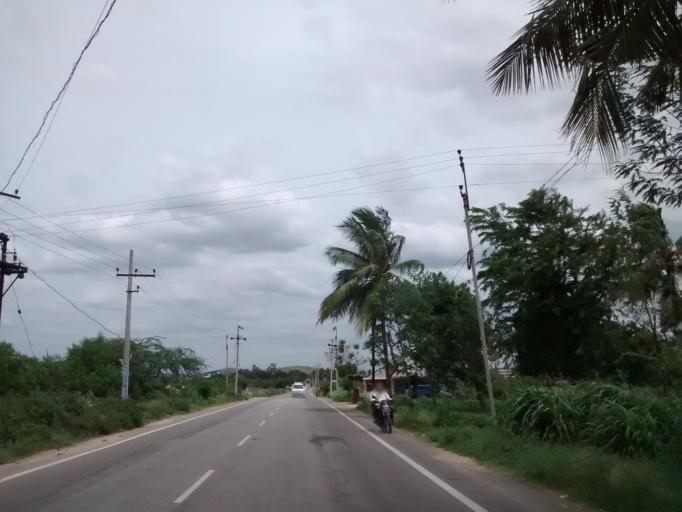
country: IN
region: Andhra Pradesh
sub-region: Chittoor
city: Chittoor
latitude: 13.2841
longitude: 79.0403
